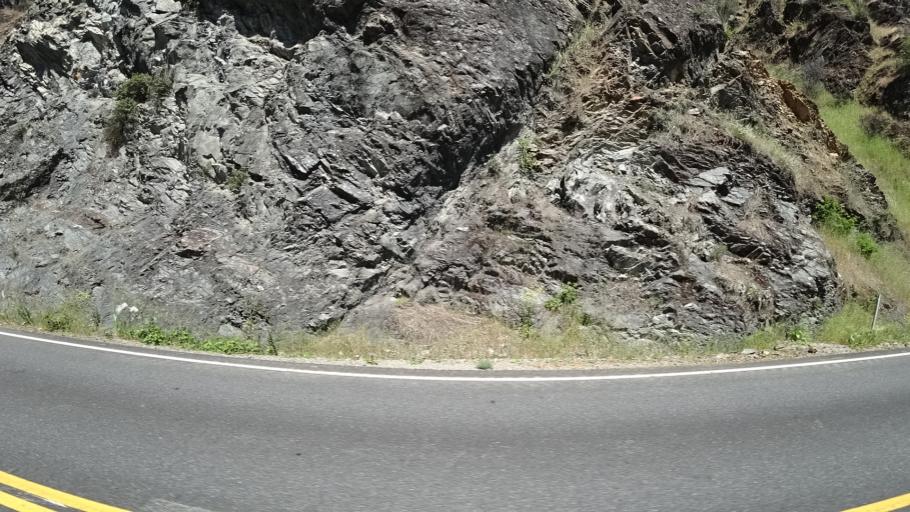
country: US
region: California
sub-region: Trinity County
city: Weaverville
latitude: 40.7373
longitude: -123.0583
